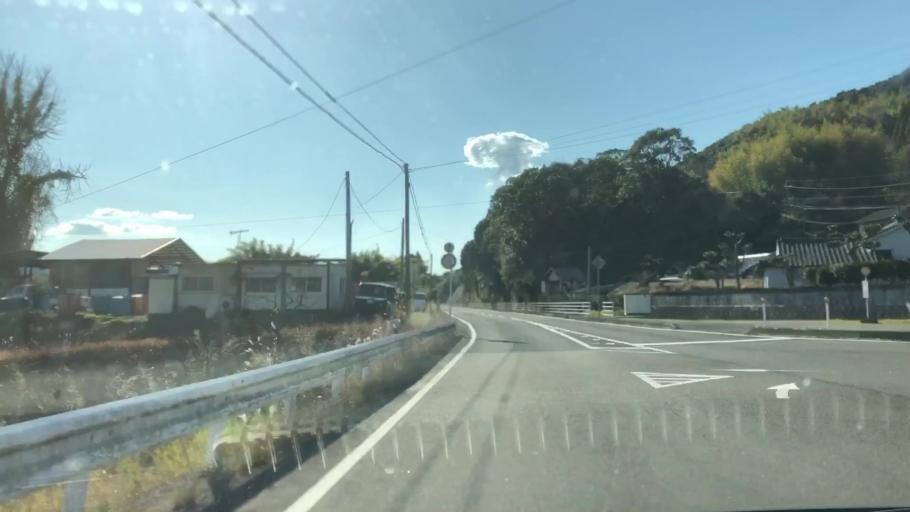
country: JP
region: Kagoshima
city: Satsumasendai
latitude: 31.8669
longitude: 130.4228
